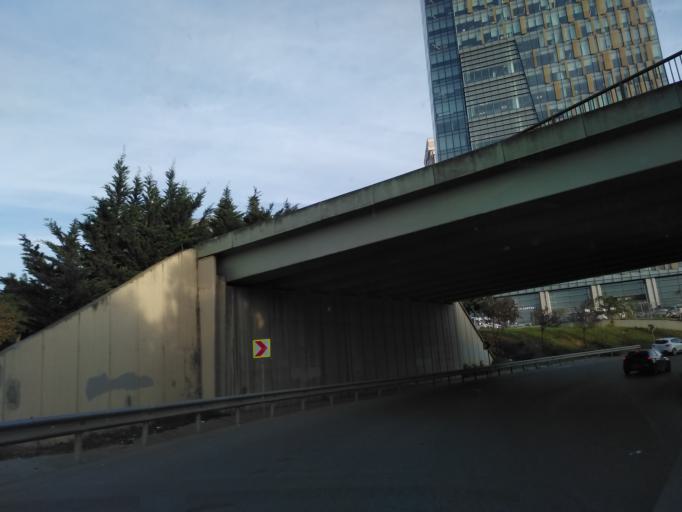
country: TR
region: Istanbul
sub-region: Atasehir
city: Atasehir
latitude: 40.9820
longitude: 29.0995
